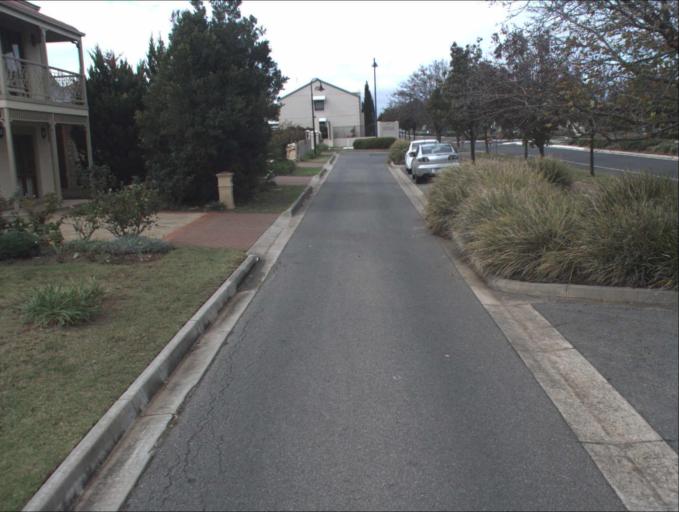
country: AU
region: South Australia
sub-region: Port Adelaide Enfield
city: Gilles Plains
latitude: -34.8579
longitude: 138.6316
